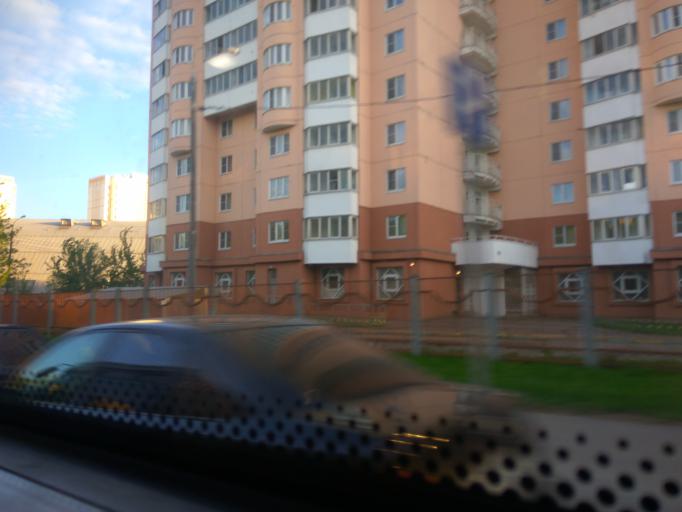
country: RU
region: Moscow
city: Tsaritsyno
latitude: 55.6460
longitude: 37.6509
